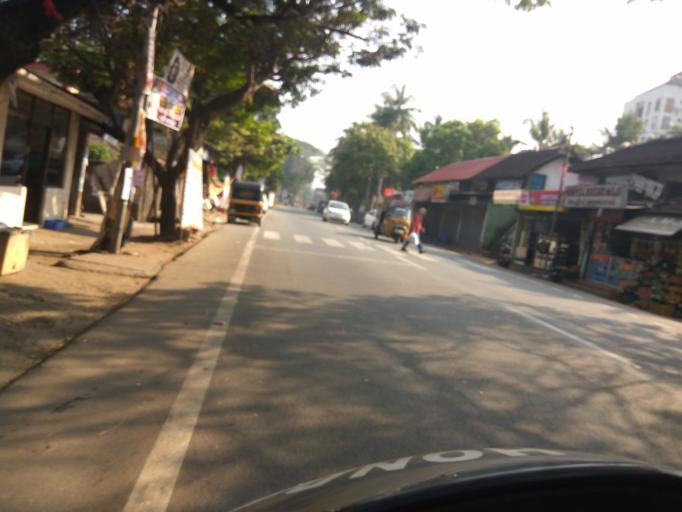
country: IN
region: Kerala
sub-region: Kozhikode
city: Kozhikode
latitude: 11.2799
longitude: 75.7707
